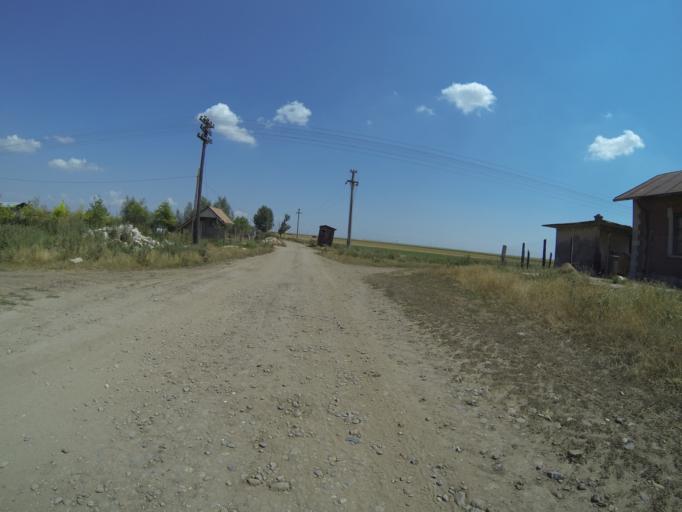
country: RO
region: Dolj
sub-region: Comuna Segarcea
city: Segarcea
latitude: 44.0829
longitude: 23.7276
